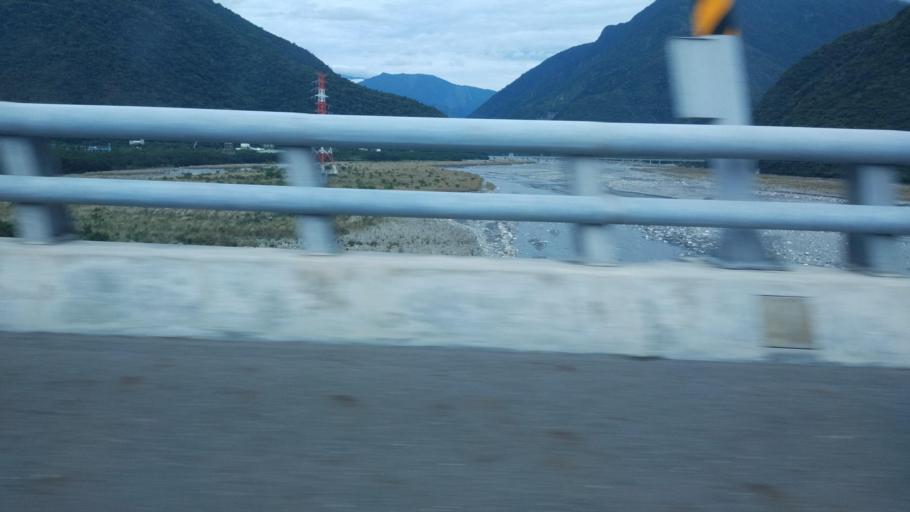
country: TW
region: Taiwan
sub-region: Hualien
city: Hualian
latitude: 24.3137
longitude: 121.7606
